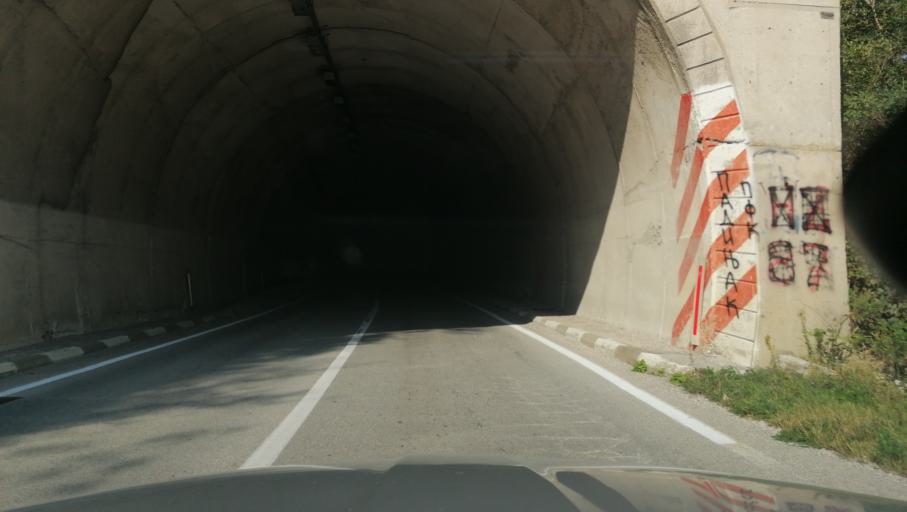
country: BA
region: Republika Srpska
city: Visegrad
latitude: 43.6988
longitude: 19.1707
